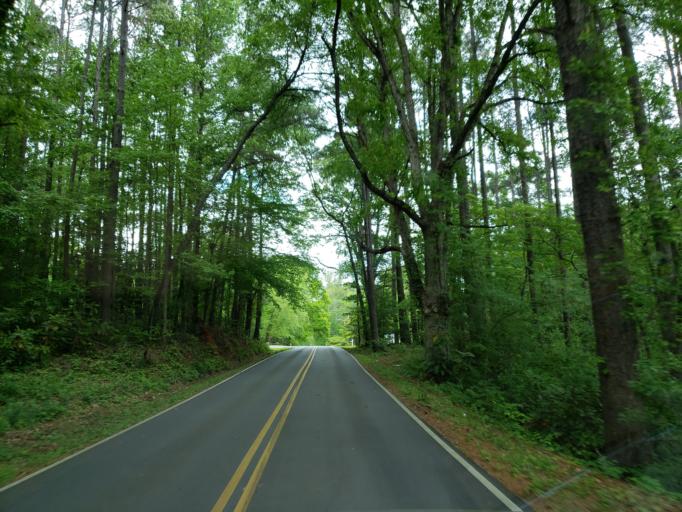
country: US
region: Georgia
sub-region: Haralson County
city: Tallapoosa
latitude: 33.7517
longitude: -85.2880
